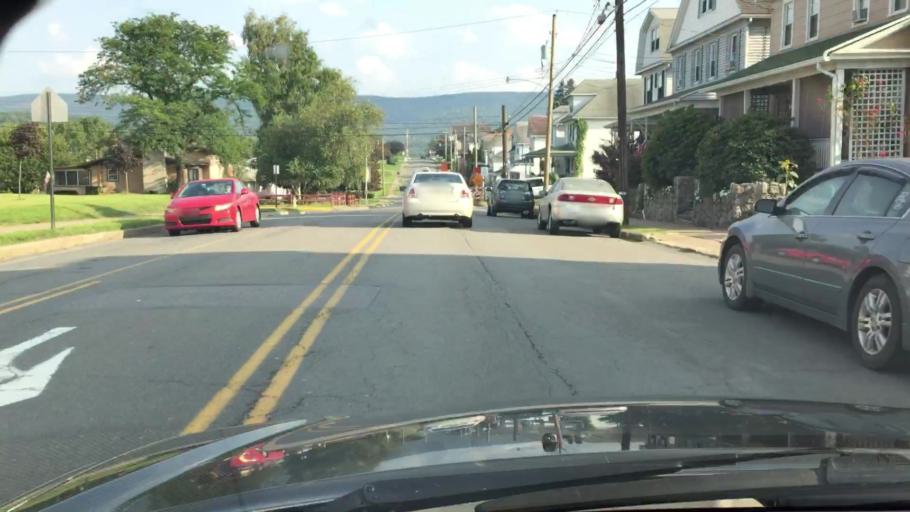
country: US
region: Pennsylvania
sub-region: Luzerne County
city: Nanticoke
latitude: 41.2021
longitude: -75.9916
